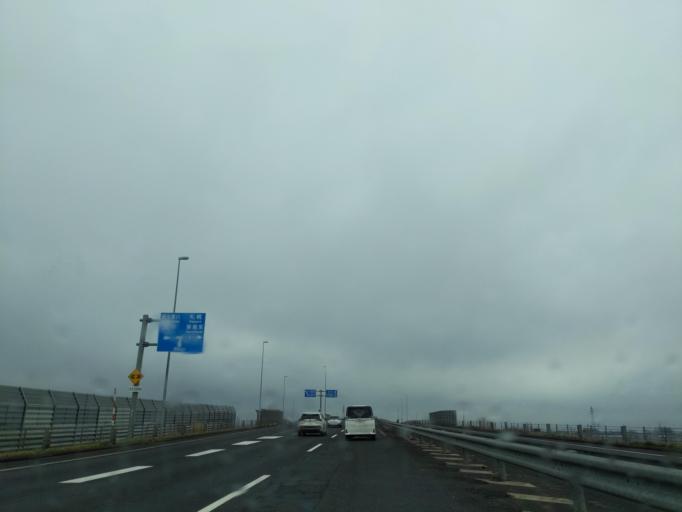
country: JP
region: Hokkaido
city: Tobetsu
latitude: 43.1837
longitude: 141.5196
